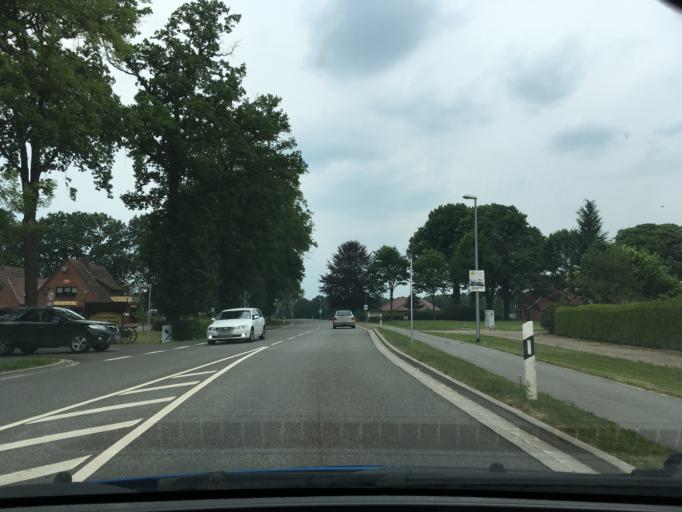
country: DE
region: Lower Saxony
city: Wenzendorf
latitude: 53.3779
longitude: 9.8034
